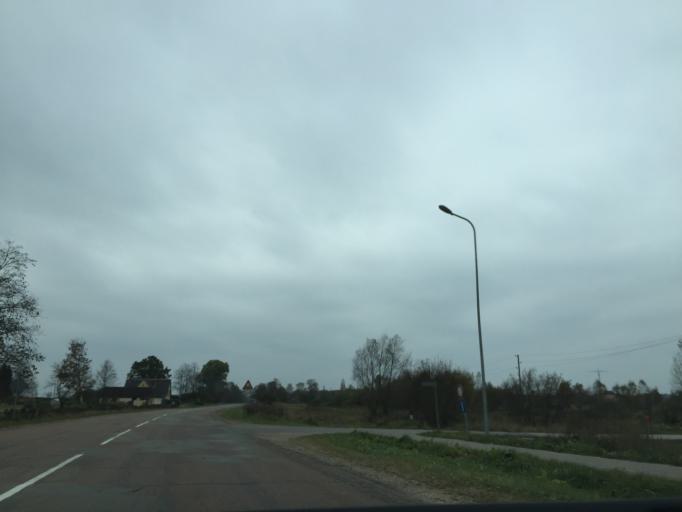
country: LV
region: Marupe
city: Marupe
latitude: 56.8451
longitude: 24.0461
